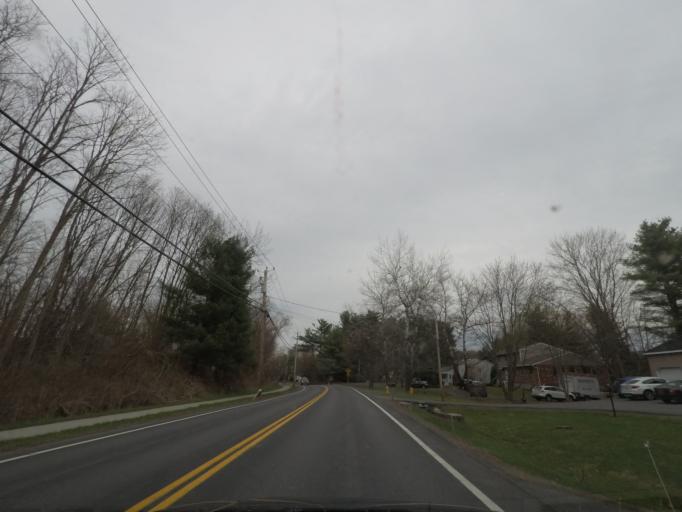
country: US
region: New York
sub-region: Albany County
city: Delmar
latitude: 42.6021
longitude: -73.8050
